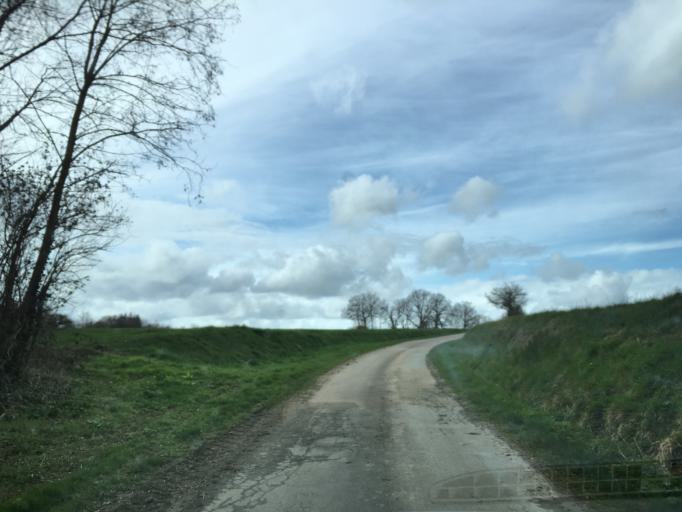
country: FR
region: Bourgogne
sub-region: Departement de l'Yonne
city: Fleury-la-Vallee
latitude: 47.8446
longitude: 3.4110
